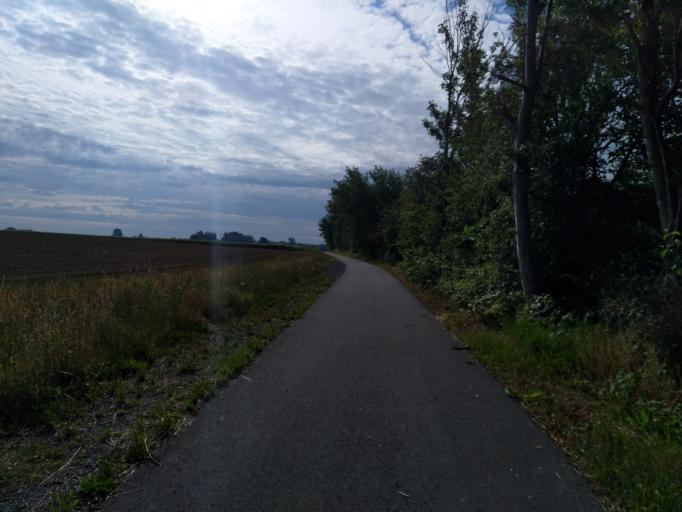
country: BE
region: Wallonia
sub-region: Province du Hainaut
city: Erquelinnes
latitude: 50.3155
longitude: 4.1078
